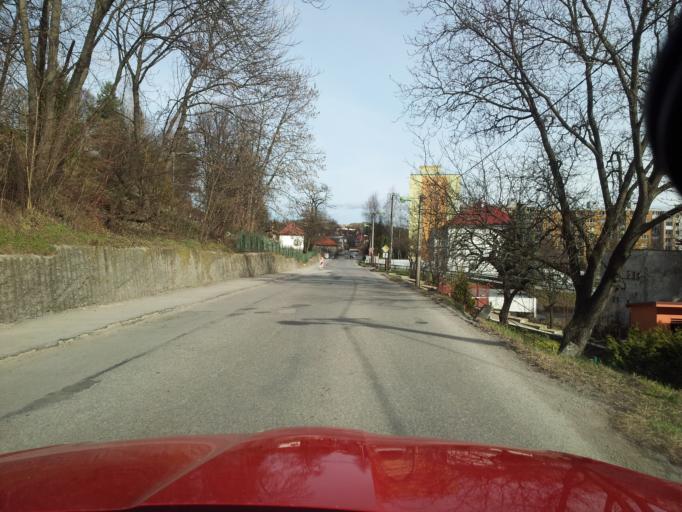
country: SK
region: Banskobystricky
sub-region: Okres Banska Bystrica
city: Banska Bystrica
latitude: 48.7436
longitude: 19.1056
